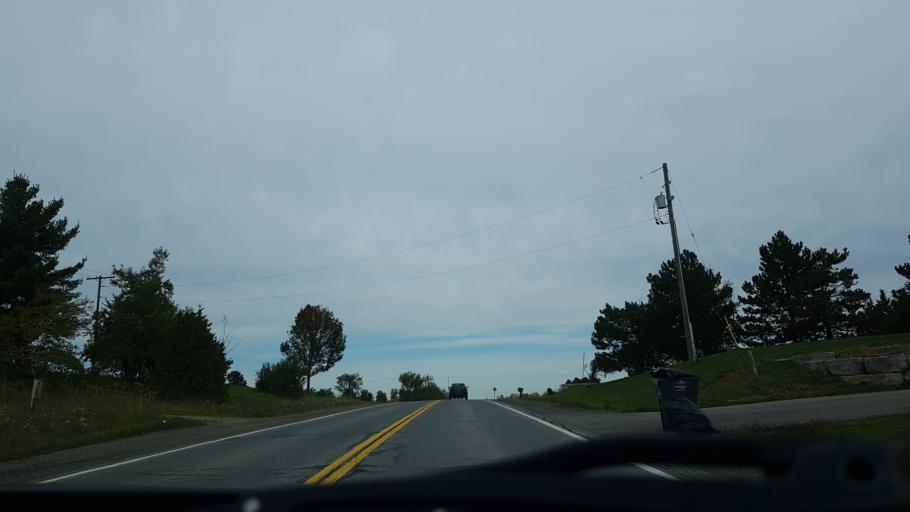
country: CA
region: Ontario
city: Orangeville
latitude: 43.8908
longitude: -79.9618
